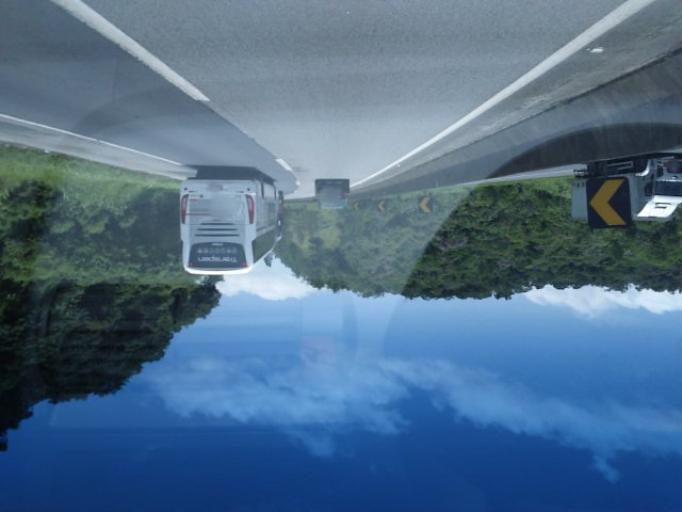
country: BR
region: Sao Paulo
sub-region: Juquia
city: Juquia
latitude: -24.3983
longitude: -47.7309
